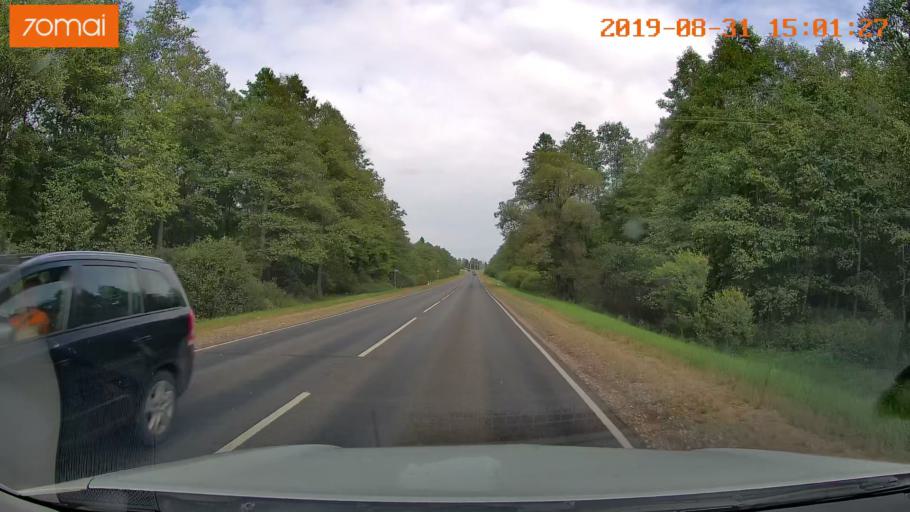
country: RU
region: Kaluga
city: Spas-Demensk
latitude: 54.3394
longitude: 34.0567
